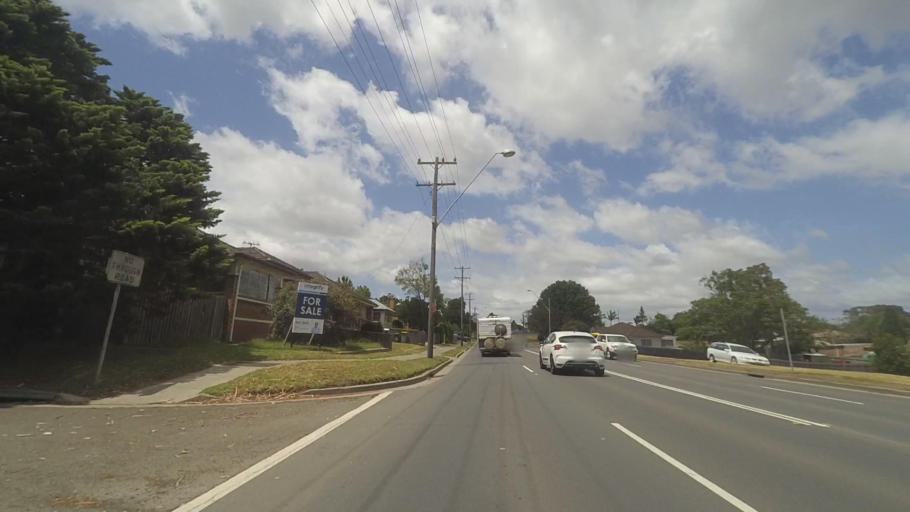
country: AU
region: New South Wales
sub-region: Shoalhaven Shire
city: Nowra
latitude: -34.8810
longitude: 150.6043
